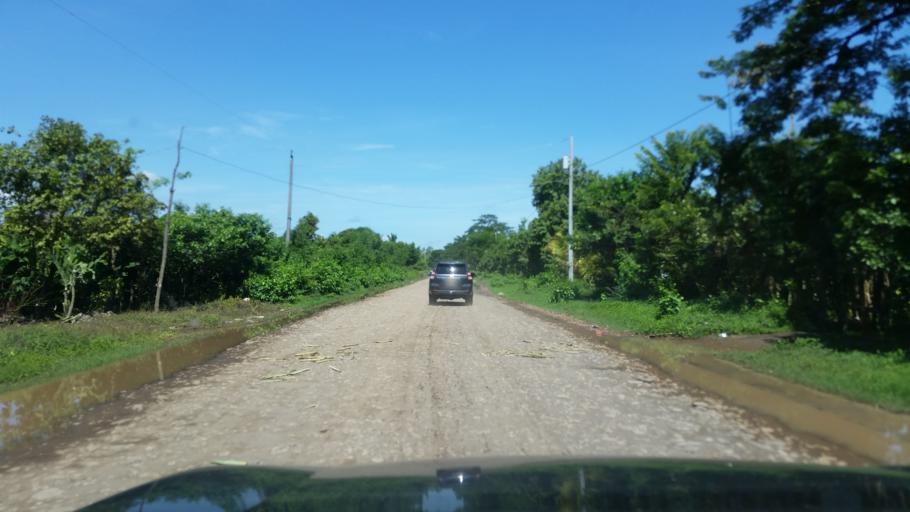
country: NI
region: Chinandega
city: Puerto Morazan
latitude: 12.7721
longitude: -87.1292
